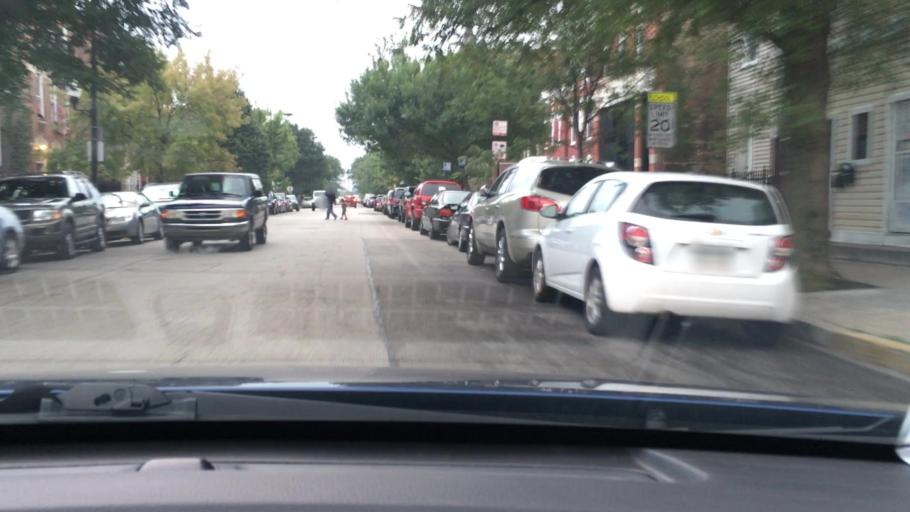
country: US
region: Illinois
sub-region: Cook County
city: Chicago
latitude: 41.8571
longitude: -87.6577
